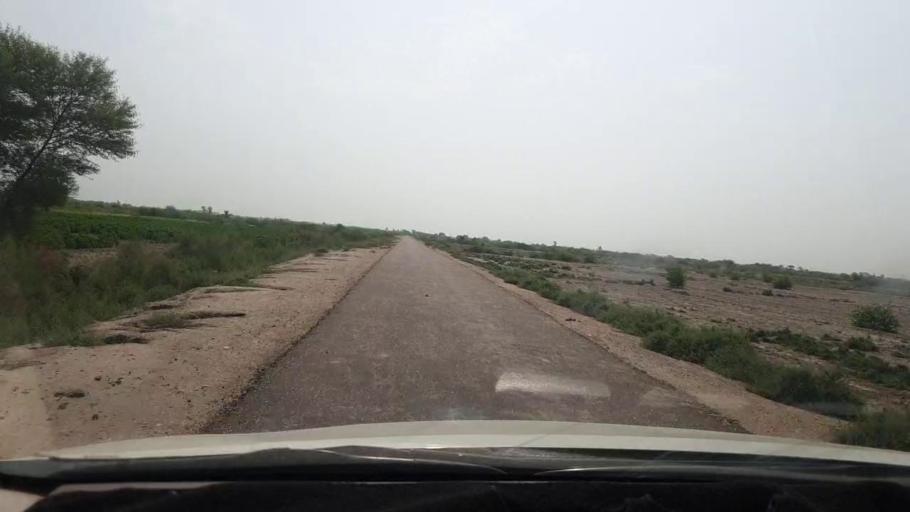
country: PK
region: Sindh
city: Rohri
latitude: 27.6046
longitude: 69.0287
